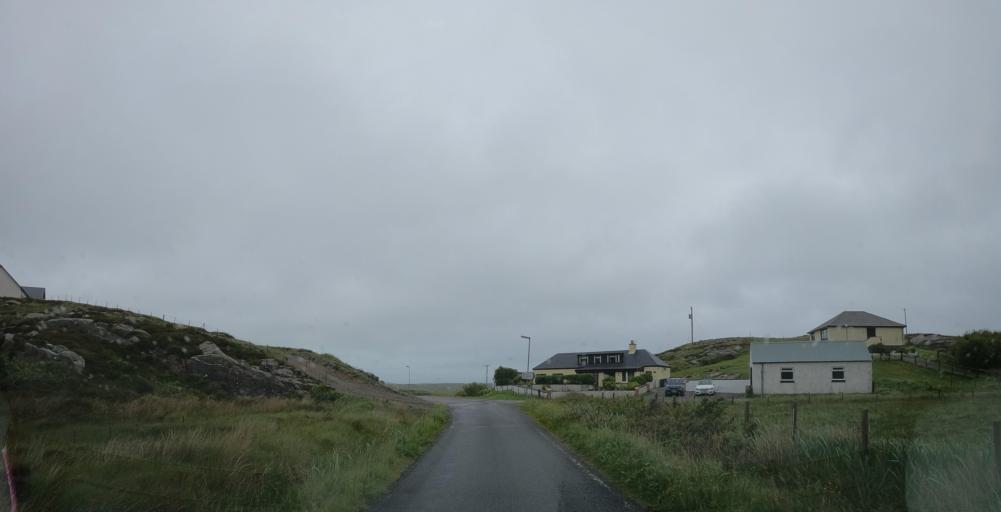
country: GB
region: Scotland
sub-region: Eilean Siar
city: Barra
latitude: 56.9960
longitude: -7.4191
